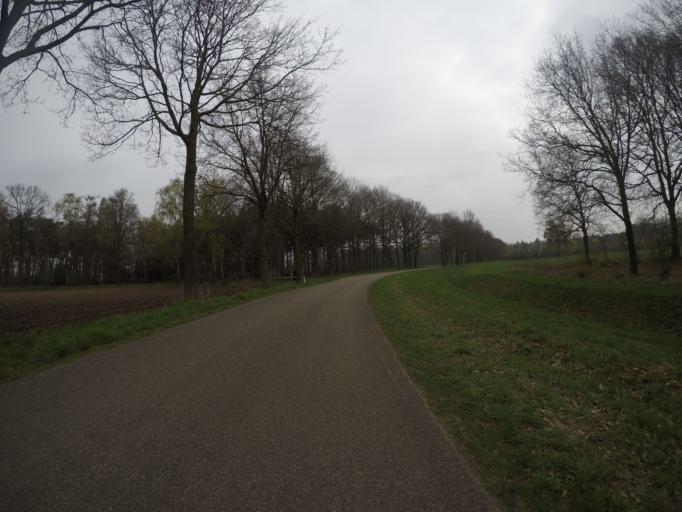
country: NL
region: Gelderland
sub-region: Gemeente Aalten
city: Aalten
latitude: 51.8902
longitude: 6.5655
